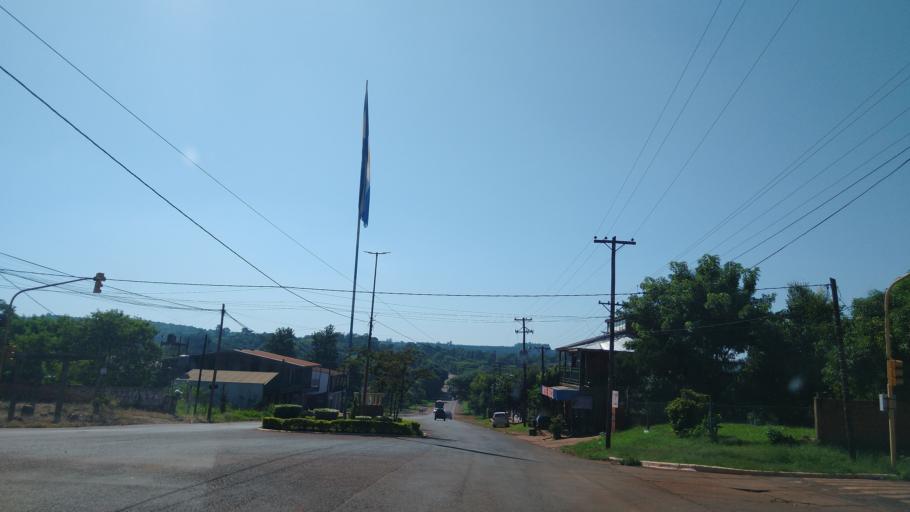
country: AR
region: Misiones
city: Puerto Esperanza
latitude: -26.0225
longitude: -54.6047
